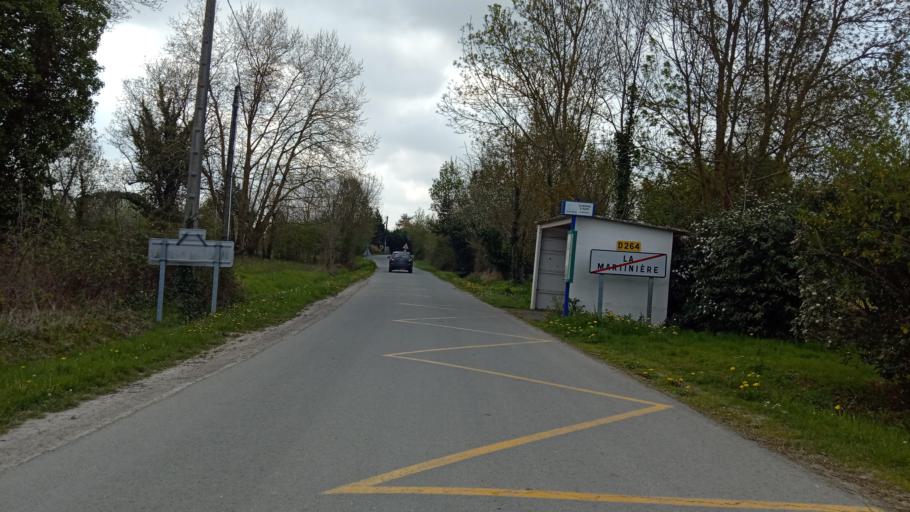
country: FR
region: Poitou-Charentes
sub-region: Departement de la Charente-Maritime
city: Verines
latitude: 46.1536
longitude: -0.9327
